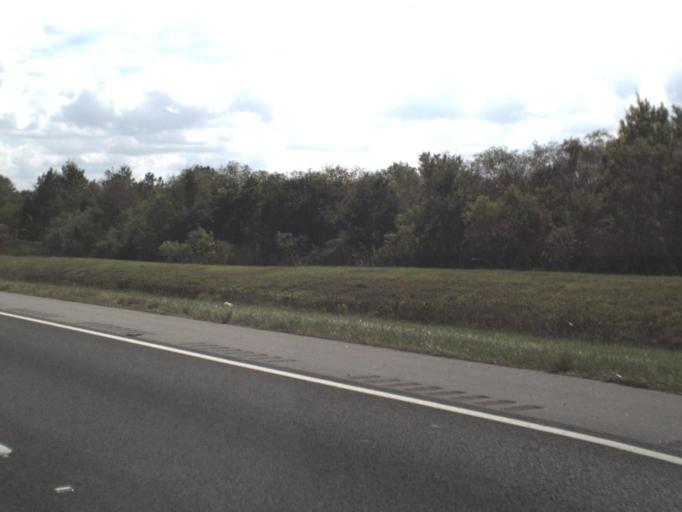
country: US
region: Florida
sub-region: Polk County
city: Highland City
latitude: 28.0095
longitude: -81.8708
